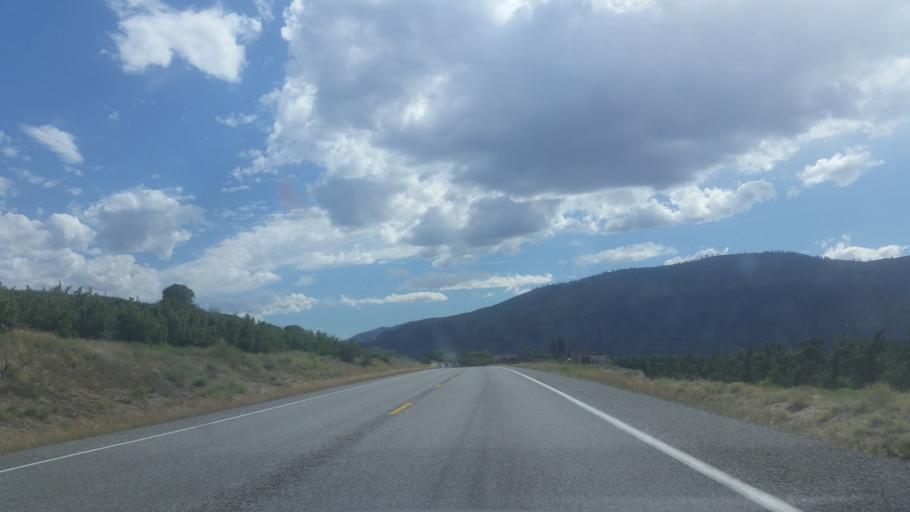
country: US
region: Washington
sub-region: Chelan County
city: Entiat
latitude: 47.7391
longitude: -120.1947
